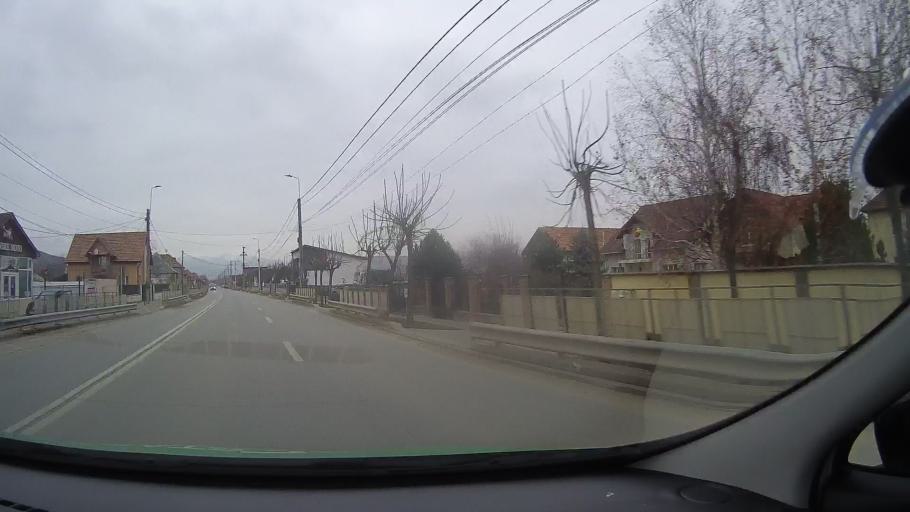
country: RO
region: Alba
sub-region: Municipiul Alba Iulia
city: Micesti
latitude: 46.0994
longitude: 23.5508
